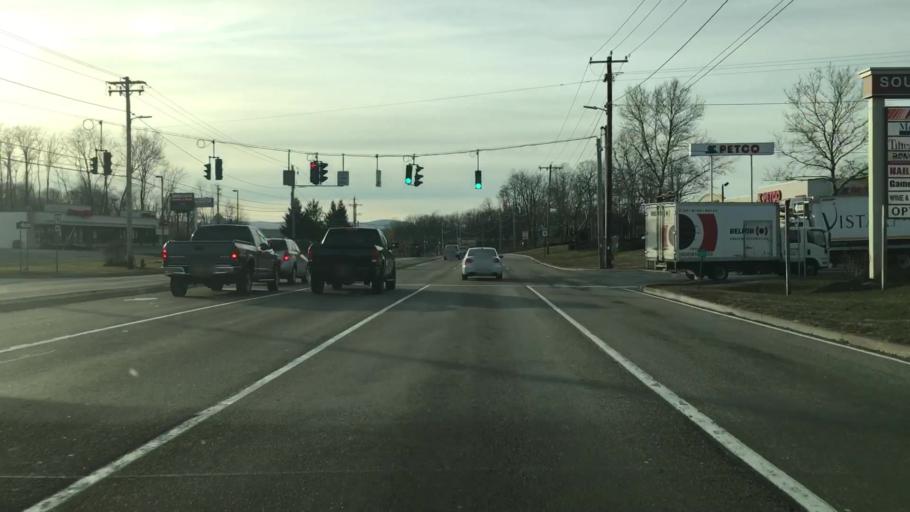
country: US
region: New York
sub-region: Dutchess County
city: Crown Heights
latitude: 41.6221
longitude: -73.9175
